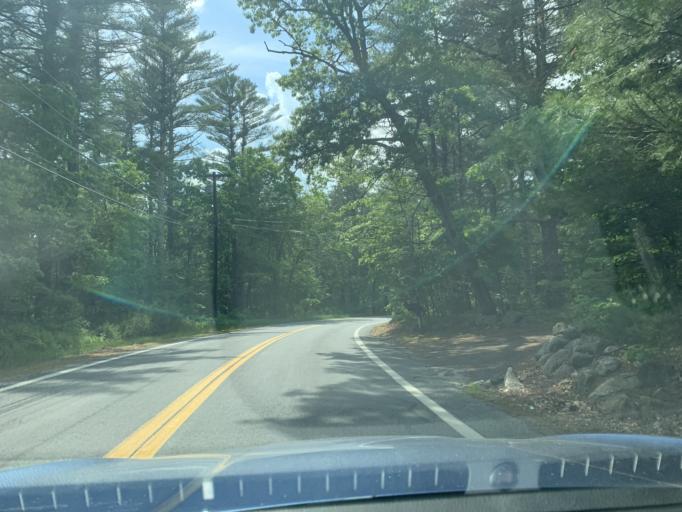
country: US
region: Rhode Island
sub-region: Kent County
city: Coventry
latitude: 41.6963
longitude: -71.7551
